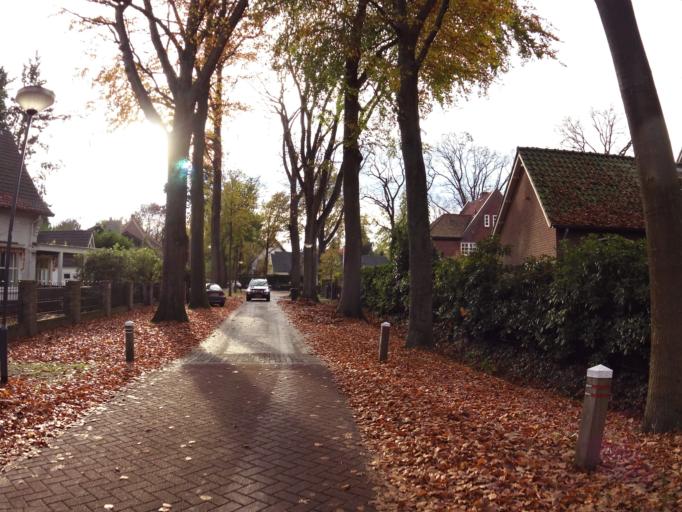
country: NL
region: North Brabant
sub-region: Gemeente Vught
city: Vught
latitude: 51.6533
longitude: 5.2760
